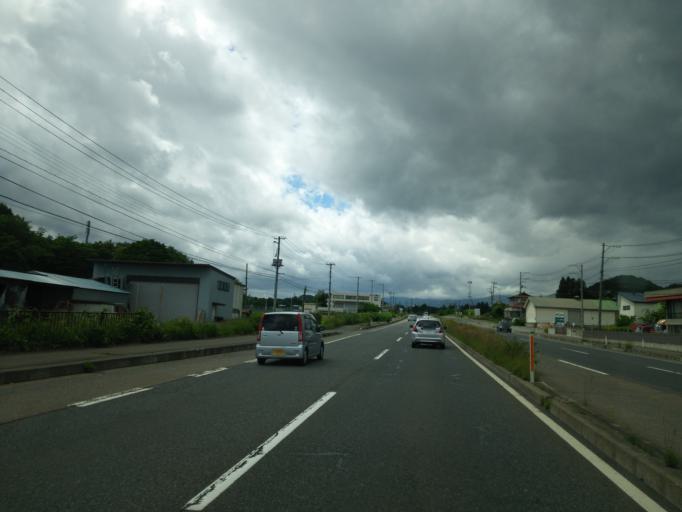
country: JP
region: Iwate
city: Shizukuishi
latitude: 39.7003
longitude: 141.0529
